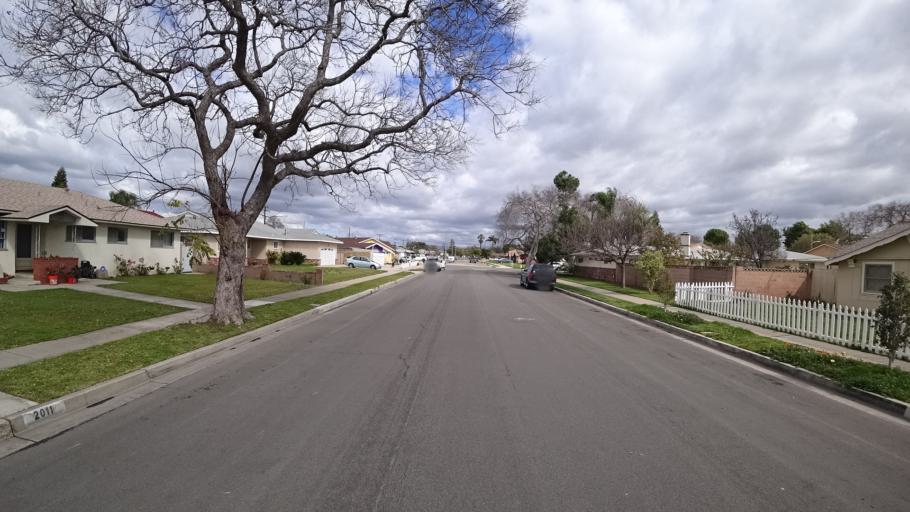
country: US
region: California
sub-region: Orange County
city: Anaheim
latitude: 33.8244
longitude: -117.9530
